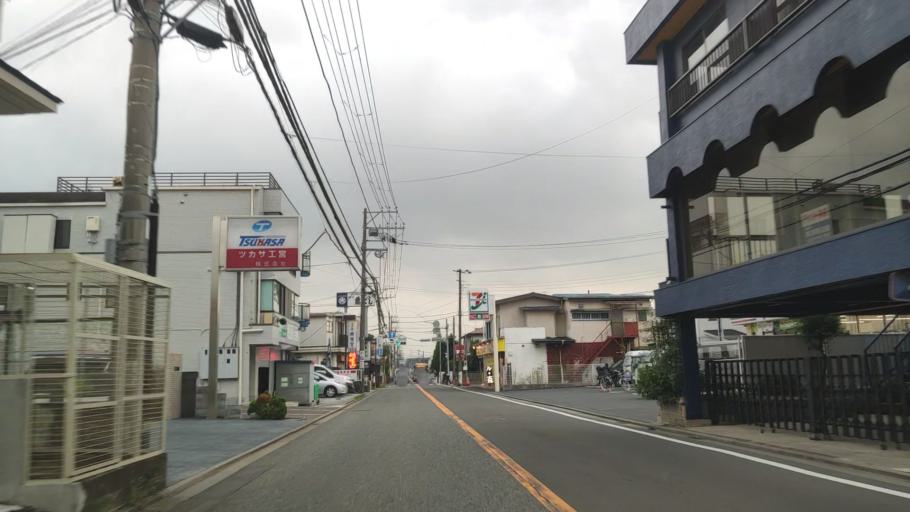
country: JP
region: Kanagawa
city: Minami-rinkan
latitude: 35.4196
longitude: 139.5005
